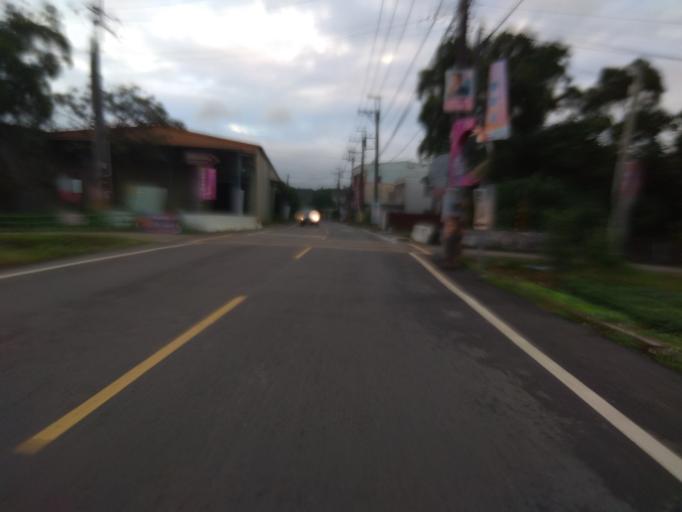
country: TW
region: Taiwan
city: Taoyuan City
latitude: 24.9466
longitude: 121.1886
